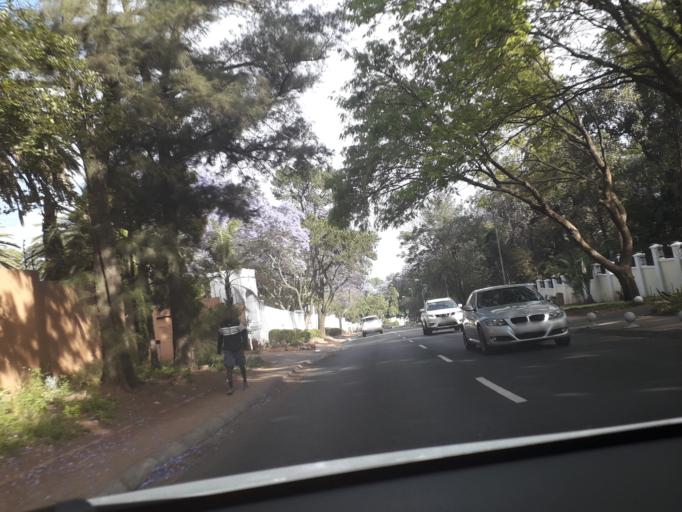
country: ZA
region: Gauteng
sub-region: City of Johannesburg Metropolitan Municipality
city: Johannesburg
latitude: -26.0705
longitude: 28.0036
